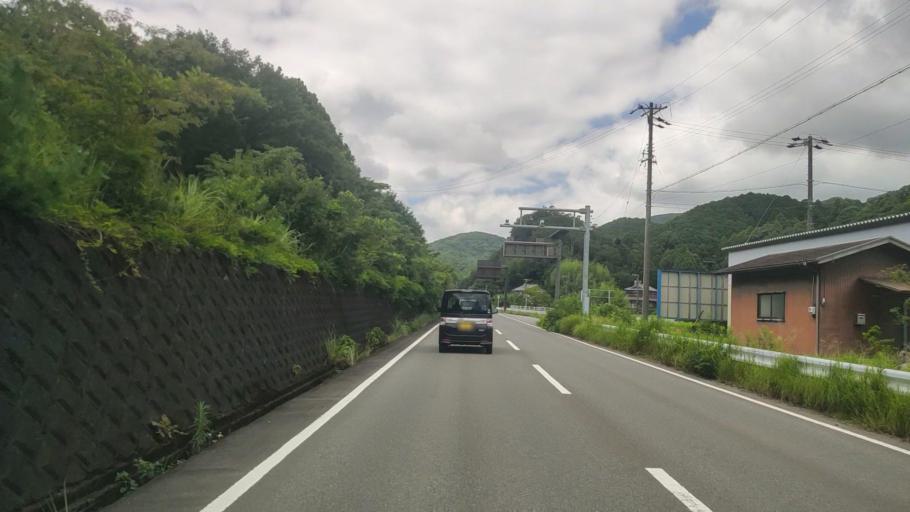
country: JP
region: Mie
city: Toba
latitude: 34.4270
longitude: 136.8247
